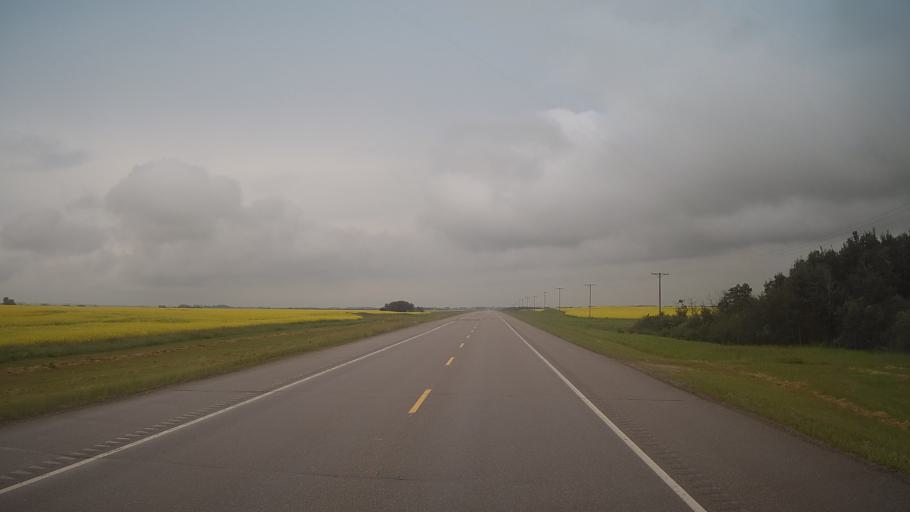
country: CA
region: Saskatchewan
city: Wilkie
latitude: 52.4265
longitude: -108.9100
